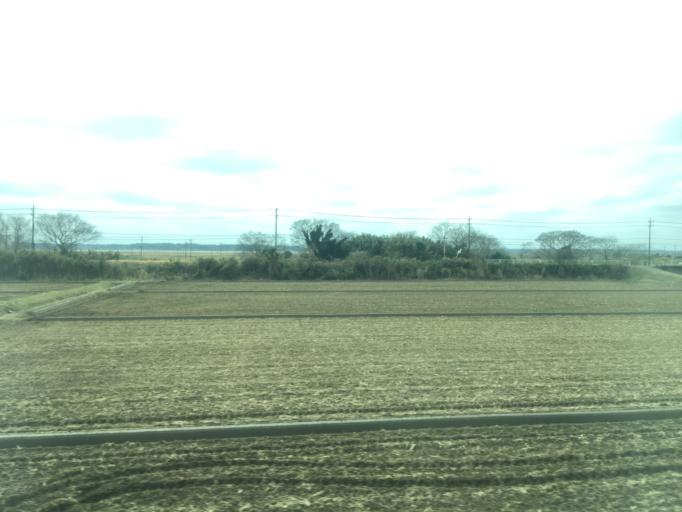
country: JP
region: Chiba
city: Narita
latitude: 35.8158
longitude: 140.2698
